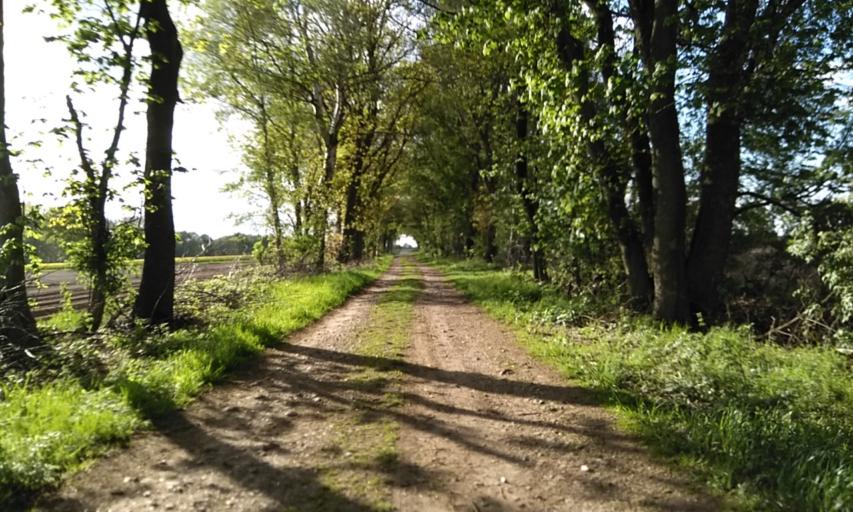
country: DE
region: Lower Saxony
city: Beckdorf
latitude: 53.4110
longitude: 9.6386
